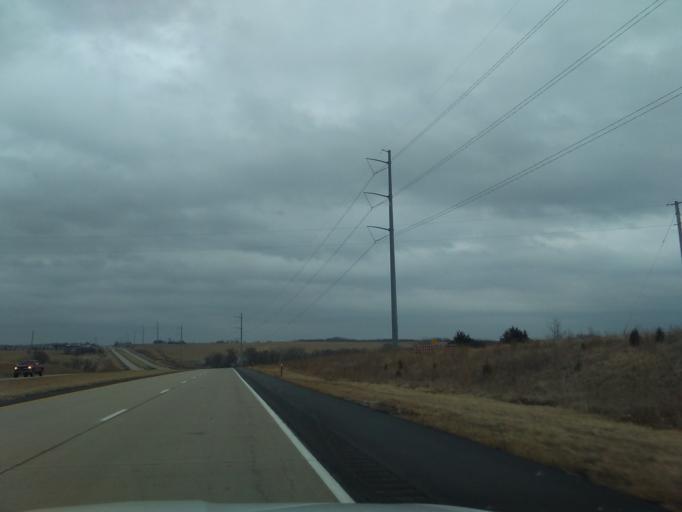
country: US
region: Nebraska
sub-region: Otoe County
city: Syracuse
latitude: 40.6685
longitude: -96.1553
